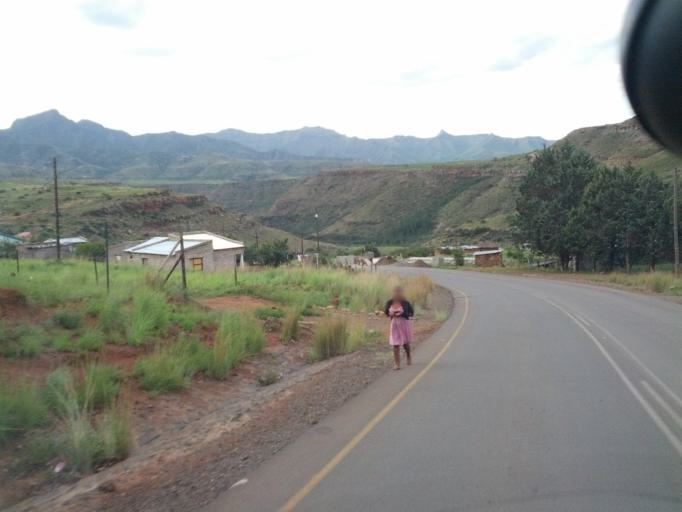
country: LS
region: Qacha's Nek
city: Qacha's Nek
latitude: -30.0730
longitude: 28.6224
